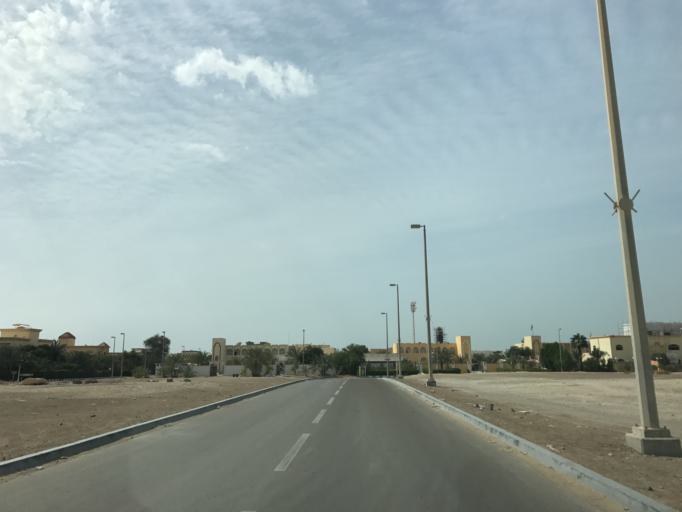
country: AE
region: Abu Dhabi
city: Abu Dhabi
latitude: 24.5560
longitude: 54.6933
